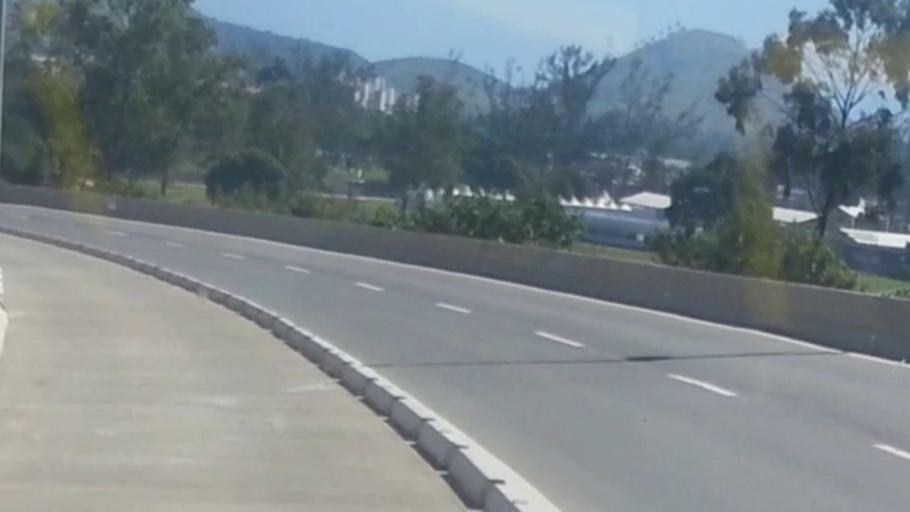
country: BR
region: Rio de Janeiro
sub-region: Nilopolis
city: Nilopolis
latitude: -22.8824
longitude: -43.4000
